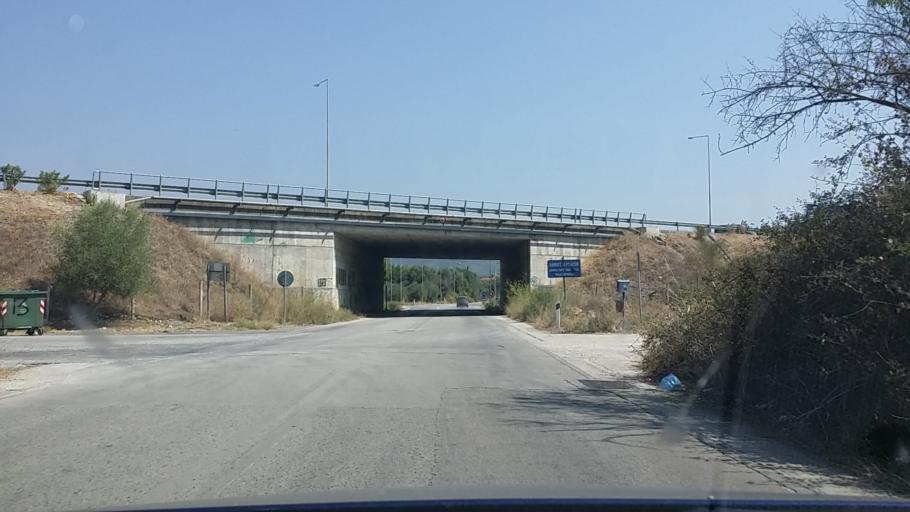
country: GR
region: Epirus
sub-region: Nomos Artas
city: Grammenitsa
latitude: 39.1726
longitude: 20.9696
